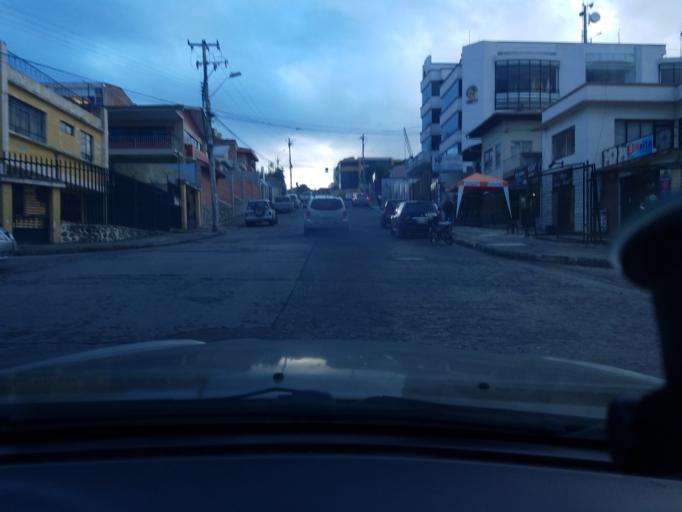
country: EC
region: Azuay
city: Cuenca
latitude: -2.8898
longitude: -79.0026
